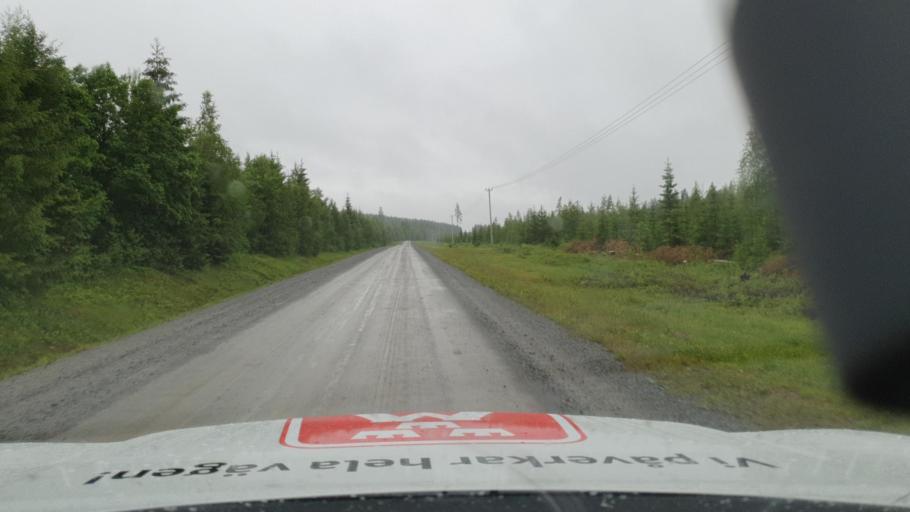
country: SE
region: Vaesterbotten
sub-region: Bjurholms Kommun
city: Bjurholm
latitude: 63.8868
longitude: 19.4272
